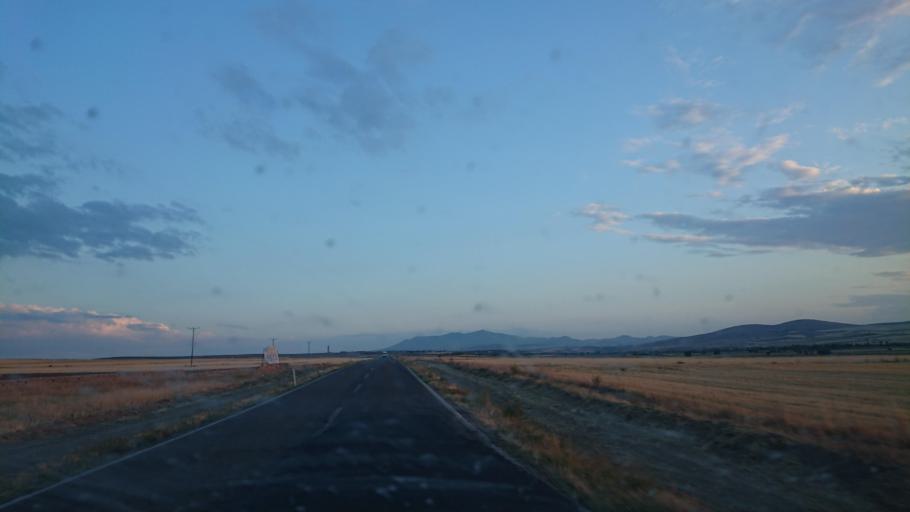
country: TR
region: Aksaray
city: Balci
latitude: 38.8229
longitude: 34.1362
